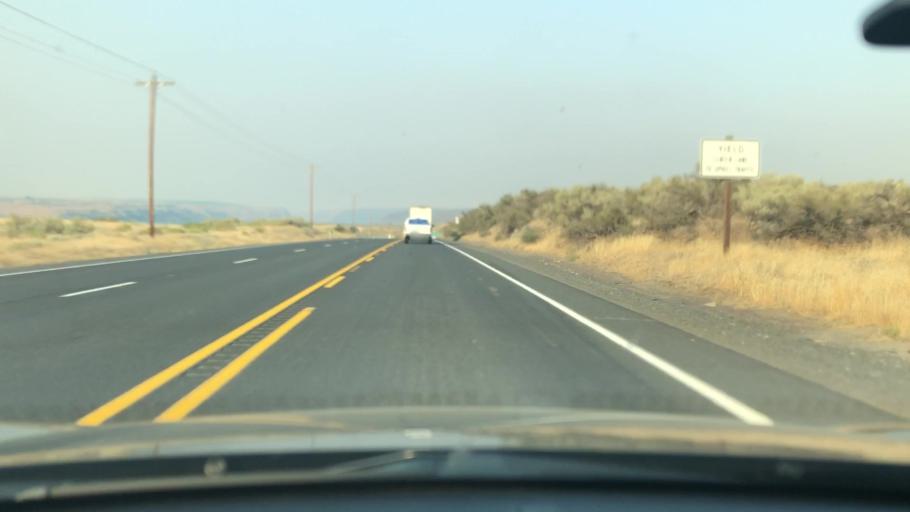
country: US
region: Oregon
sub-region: Umatilla County
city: Stanfield
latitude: 45.9111
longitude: -119.1451
